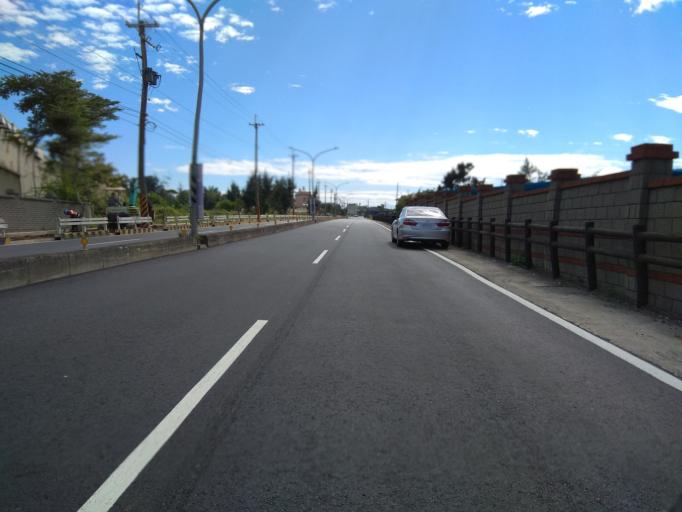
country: TW
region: Taiwan
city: Taoyuan City
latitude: 25.0588
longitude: 121.1362
